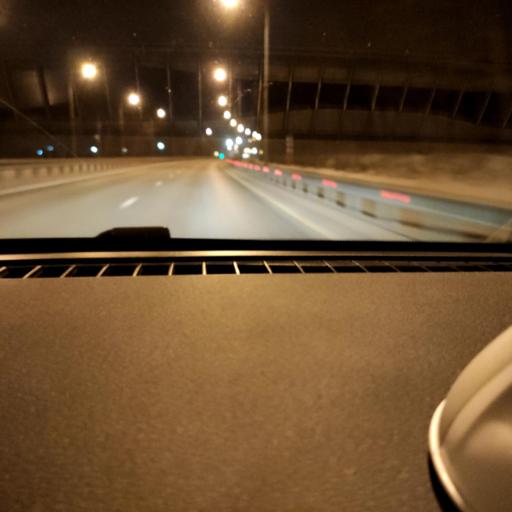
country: RU
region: Samara
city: Petra-Dubrava
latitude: 53.2846
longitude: 50.2510
